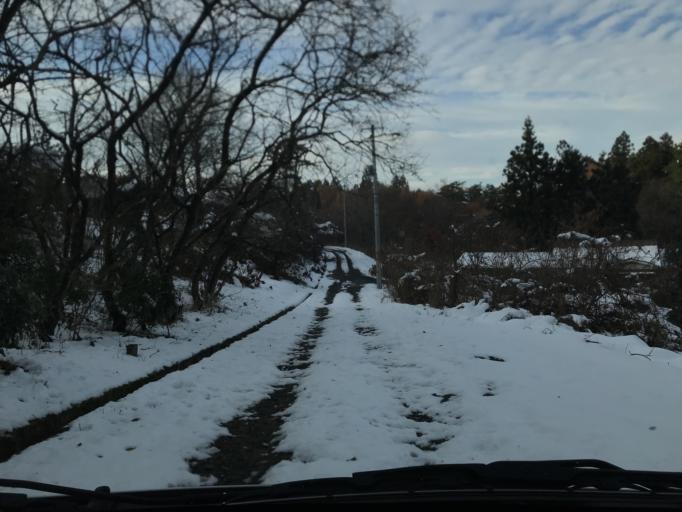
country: JP
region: Iwate
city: Mizusawa
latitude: 39.0373
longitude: 141.1042
